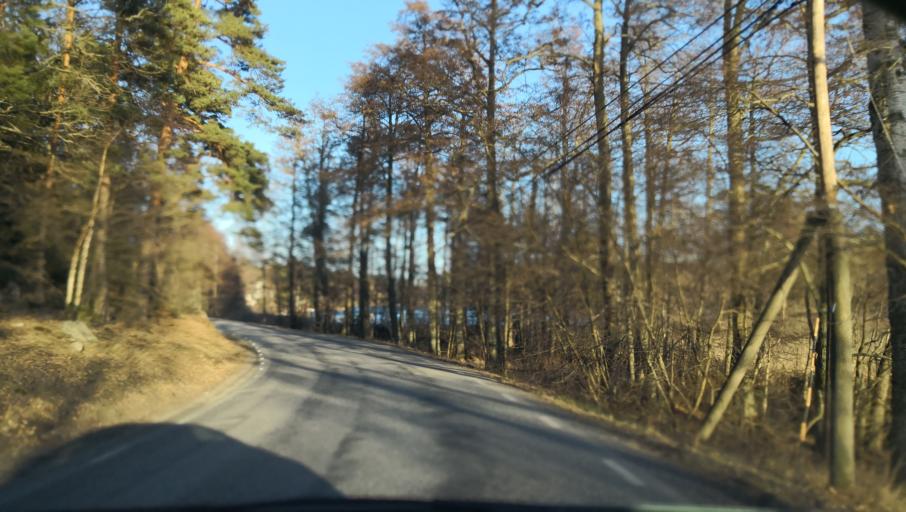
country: SE
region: Stockholm
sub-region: Varmdo Kommun
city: Gustavsberg
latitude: 59.3273
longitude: 18.4158
